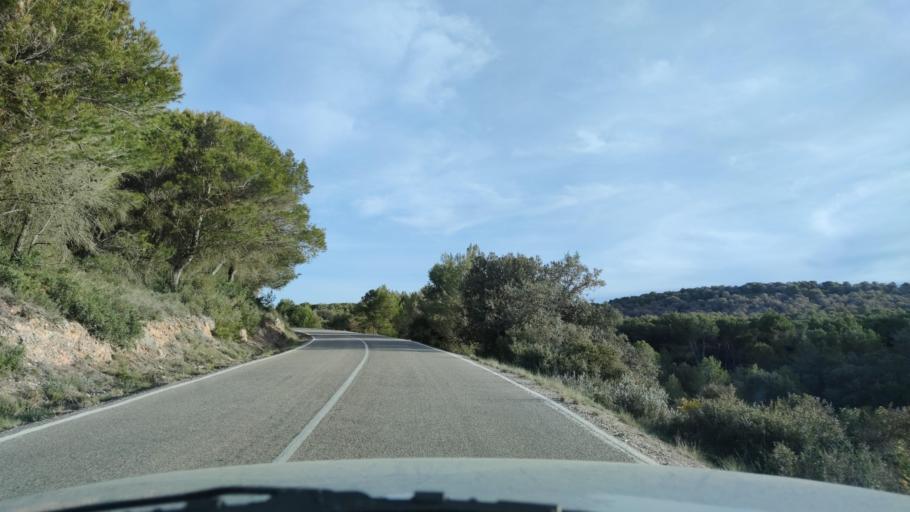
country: ES
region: Catalonia
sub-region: Provincia de Lleida
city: Castello de Farfanya
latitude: 41.8505
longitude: 0.7797
